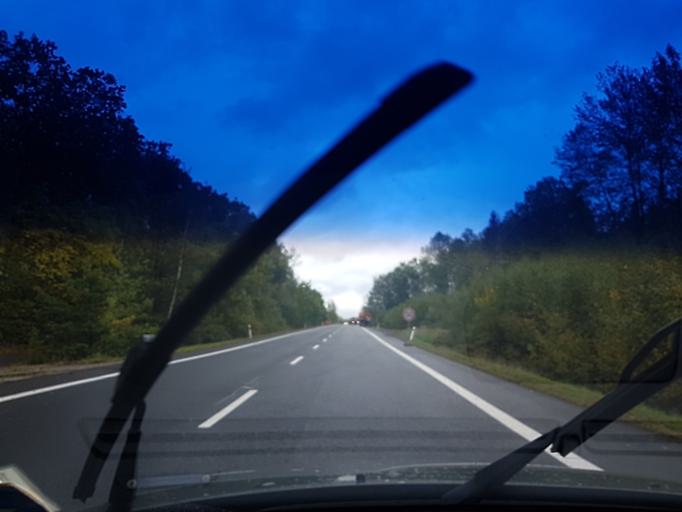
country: CZ
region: Karlovarsky
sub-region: Okres Cheb
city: Frantiskovy Lazne
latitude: 50.0816
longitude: 12.3179
